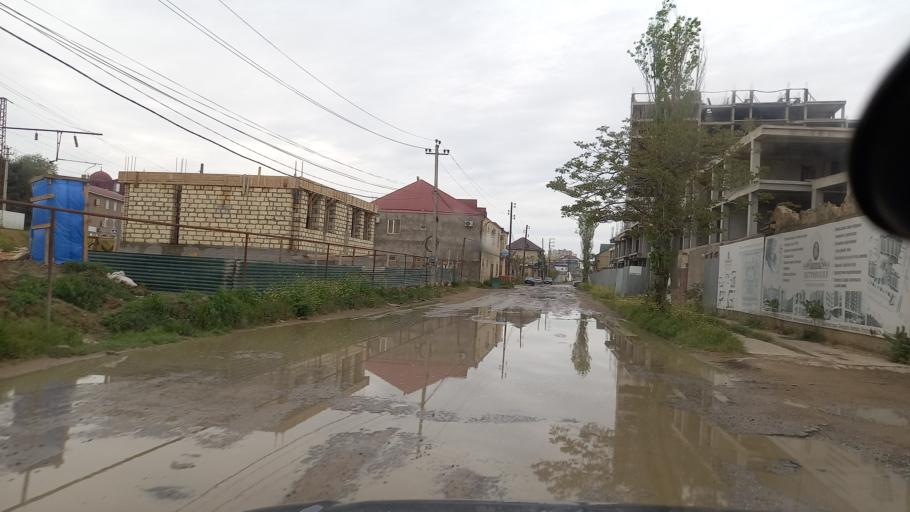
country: RU
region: Dagestan
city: Derbent
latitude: 42.0686
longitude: 48.3012
